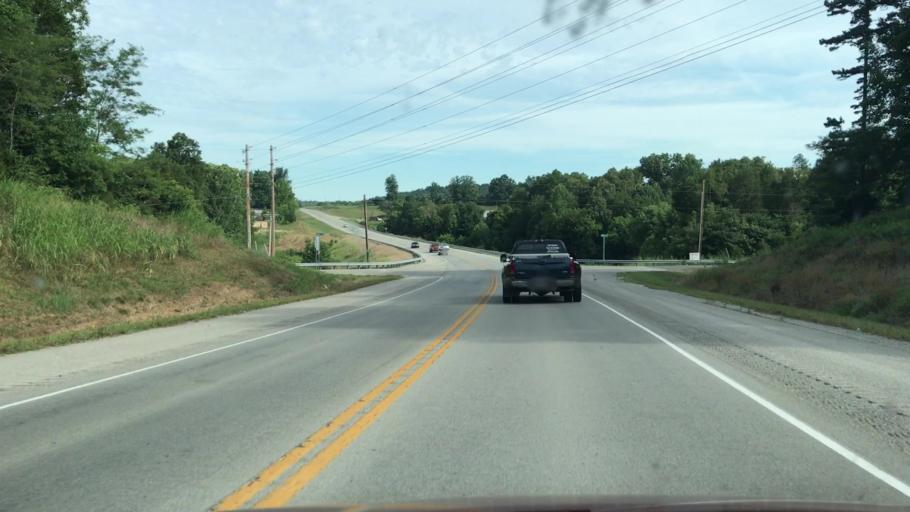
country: US
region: Kentucky
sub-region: Edmonson County
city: Brownsville
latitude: 37.1599
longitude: -86.2223
